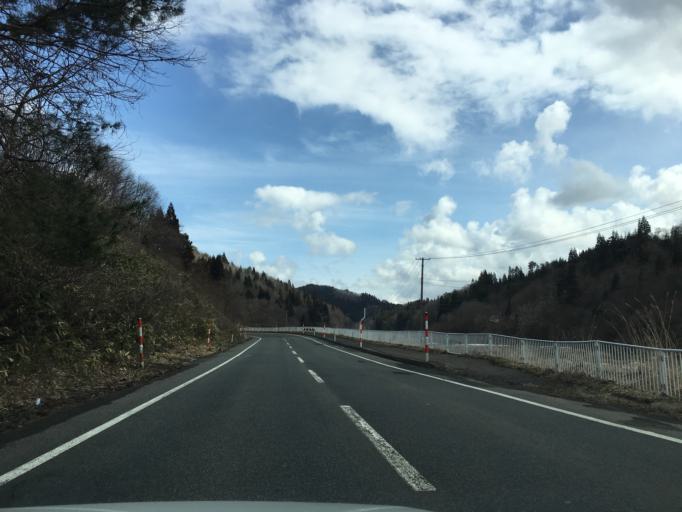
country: JP
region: Akita
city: Odate
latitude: 40.1863
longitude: 140.5096
